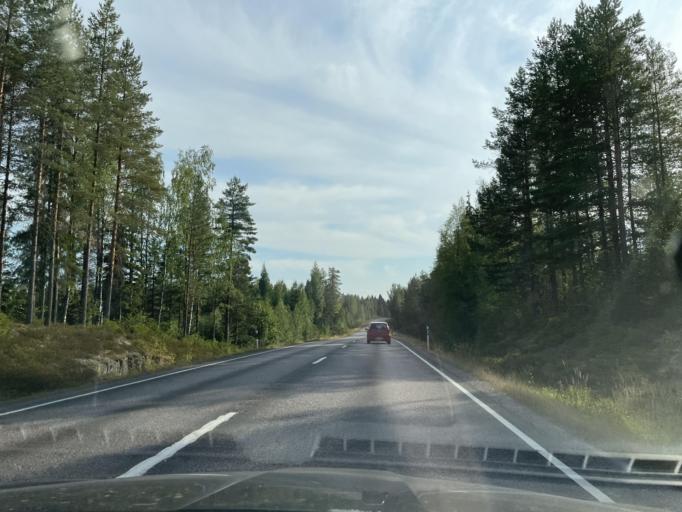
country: FI
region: Central Finland
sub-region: Jaemsae
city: Kuhmoinen
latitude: 61.6185
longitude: 25.2739
